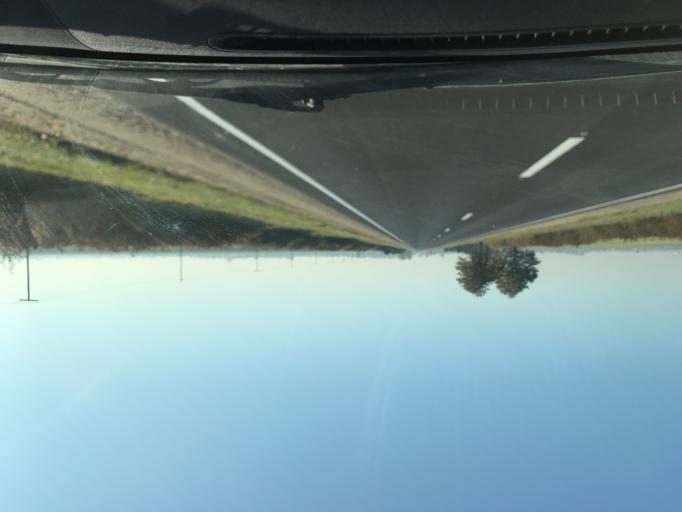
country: BY
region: Brest
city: Baranovichi
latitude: 52.8906
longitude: 25.8218
